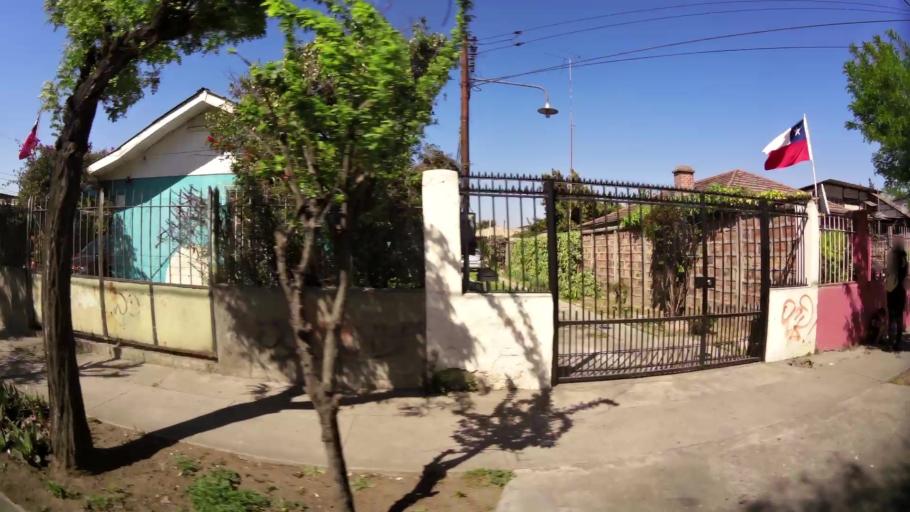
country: CL
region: Santiago Metropolitan
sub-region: Provincia de Santiago
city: Lo Prado
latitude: -33.5025
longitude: -70.7257
